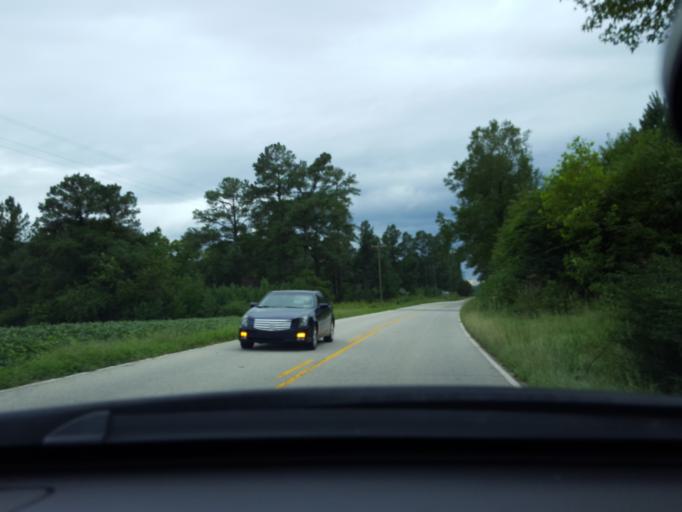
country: US
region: North Carolina
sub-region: Duplin County
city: Rose Hill
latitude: 34.8204
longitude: -78.1721
